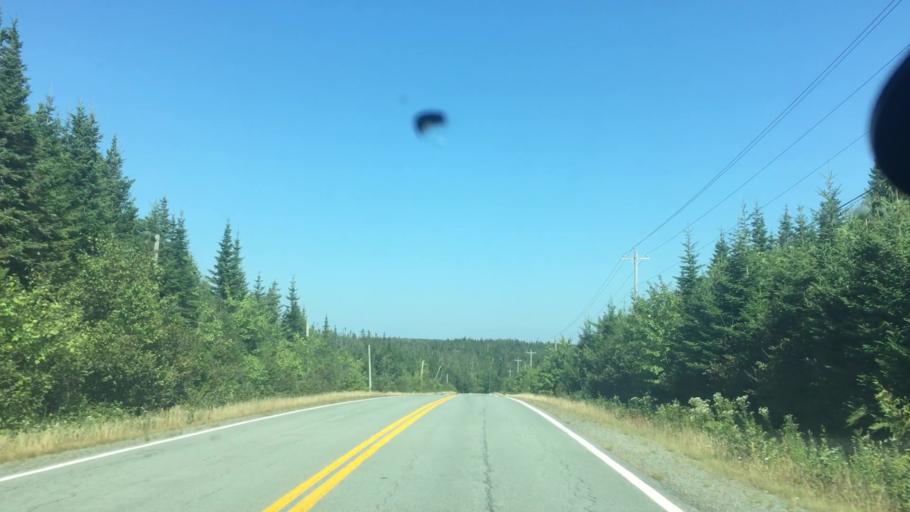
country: CA
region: Nova Scotia
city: Antigonish
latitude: 45.0097
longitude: -62.1056
